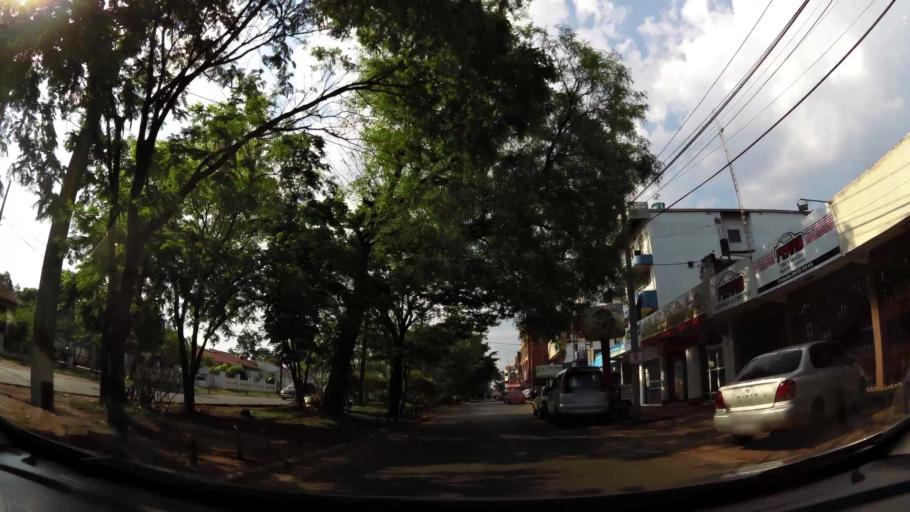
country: PY
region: Alto Parana
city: Presidente Franco
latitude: -25.5357
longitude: -54.6239
